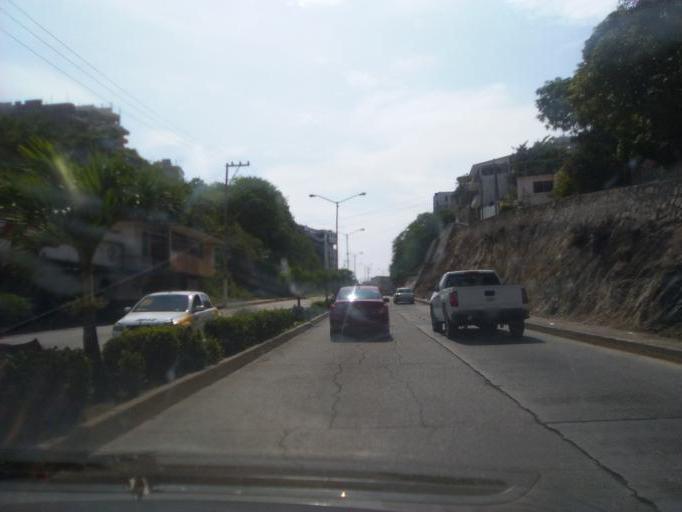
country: MX
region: Guerrero
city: Acapulco de Juarez
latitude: 16.8623
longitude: -99.9201
